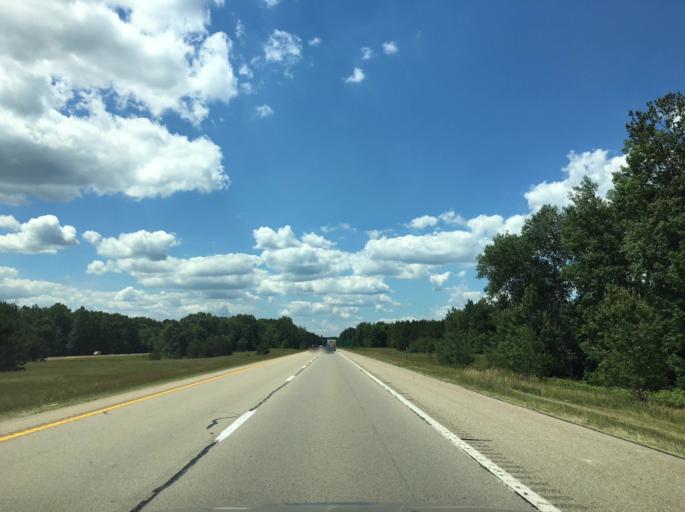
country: US
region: Michigan
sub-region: Clare County
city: Clare
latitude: 43.8735
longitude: -84.8299
